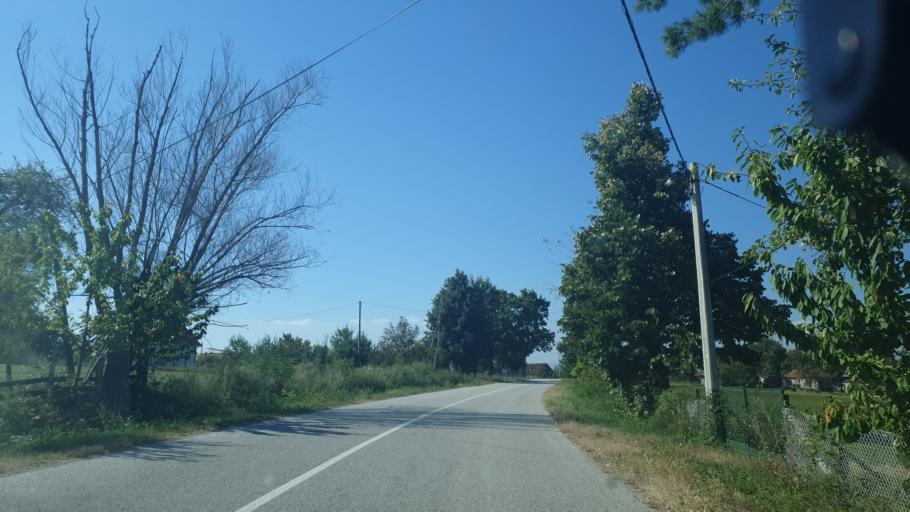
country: RS
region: Central Serbia
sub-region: Kolubarski Okrug
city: Mionica
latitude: 44.2934
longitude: 20.1330
